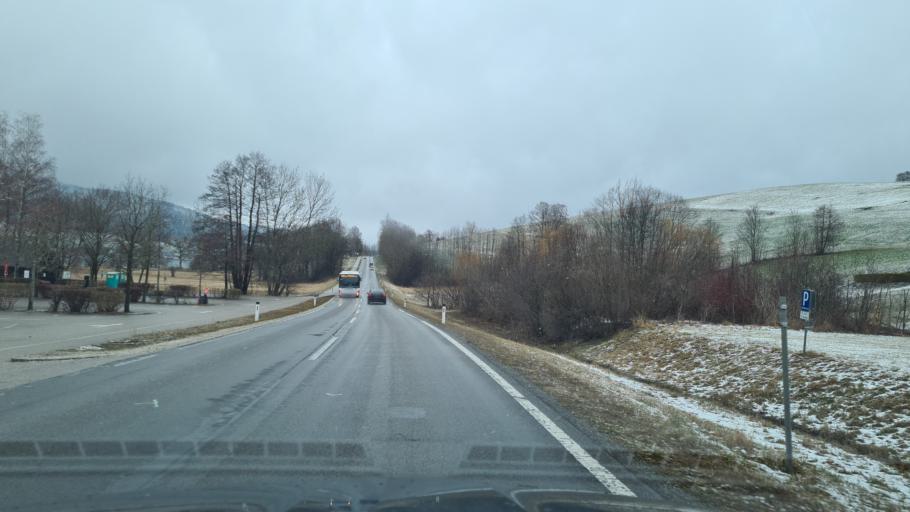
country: AT
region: Upper Austria
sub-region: Politischer Bezirk Vocklabruck
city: Zell am Moos
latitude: 47.8909
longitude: 13.3180
